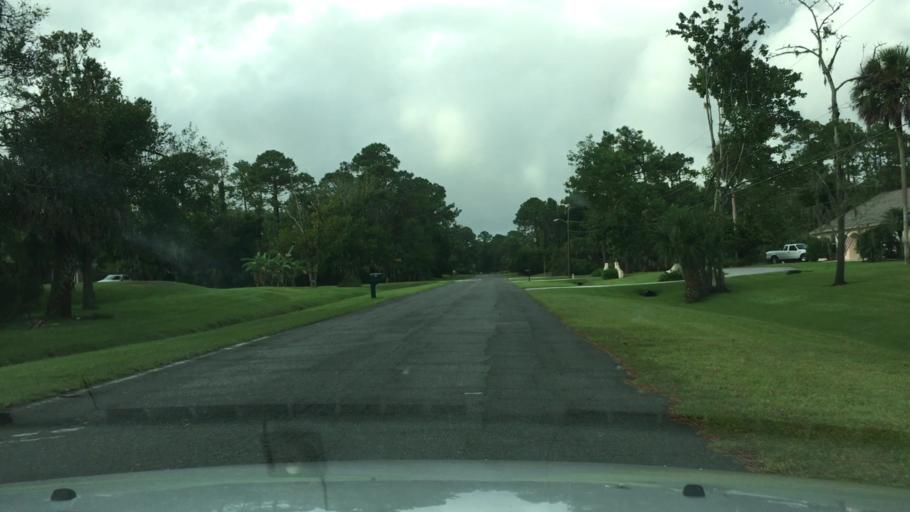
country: US
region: Florida
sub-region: Volusia County
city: Ormond-by-the-Sea
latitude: 29.3337
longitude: -81.1167
